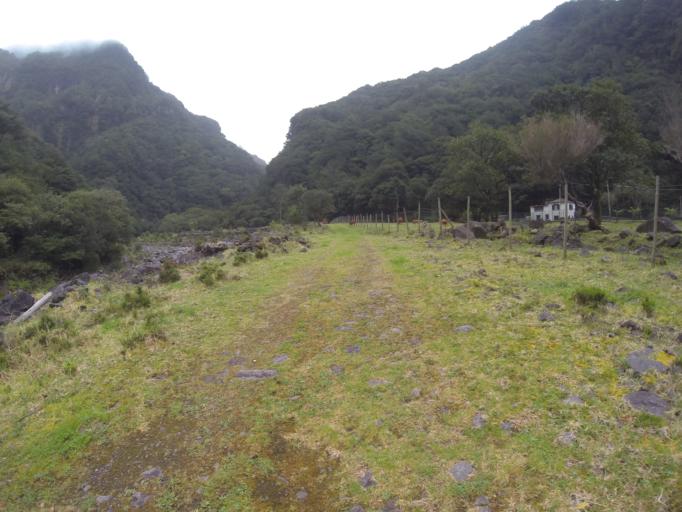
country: PT
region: Madeira
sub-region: Sao Vicente
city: Sao Vicente
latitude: 32.7960
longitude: -17.1138
